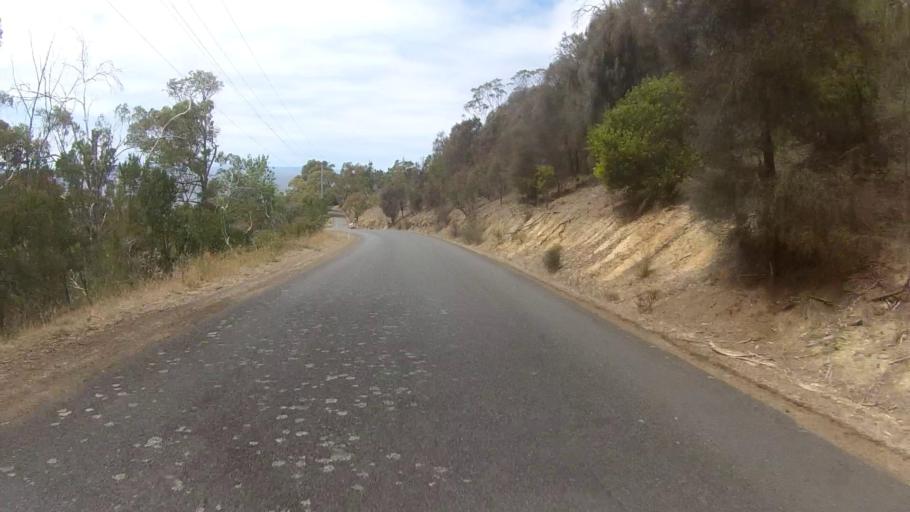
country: AU
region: Tasmania
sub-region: Kingborough
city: Blackmans Bay
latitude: -43.0367
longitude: 147.3335
